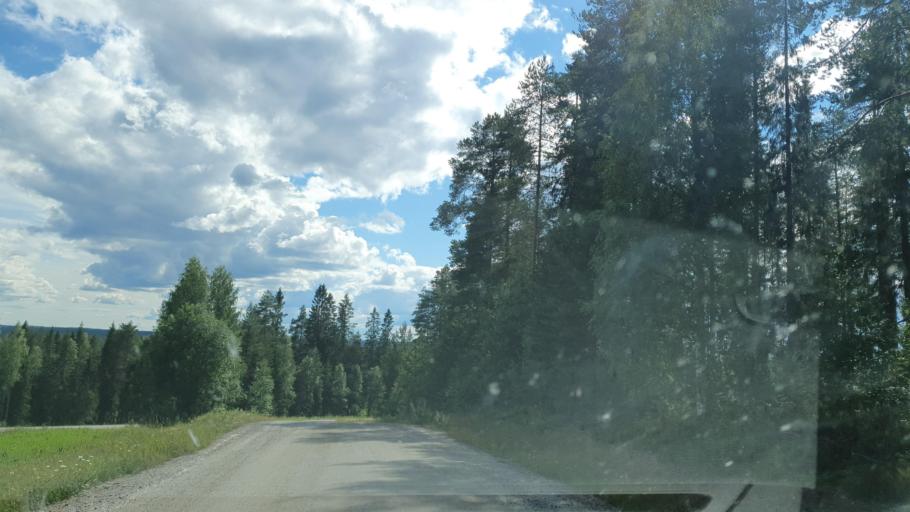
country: FI
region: Kainuu
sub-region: Kehys-Kainuu
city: Kuhmo
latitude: 64.1267
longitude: 29.6425
